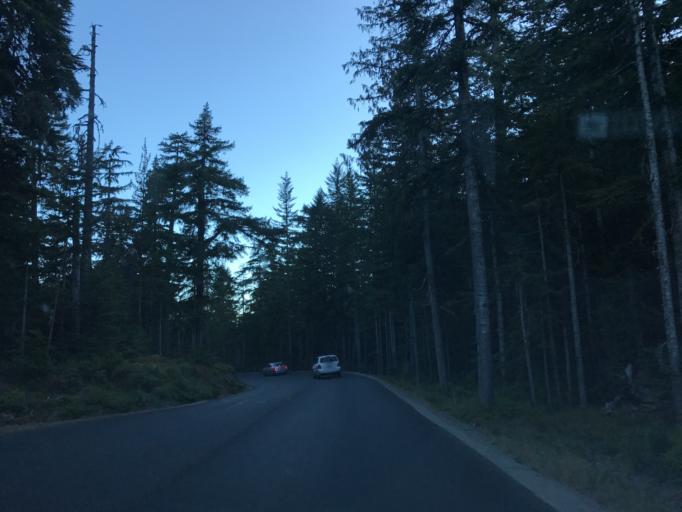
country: US
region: Washington
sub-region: Pierce County
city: Buckley
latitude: 46.7700
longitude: -121.7916
